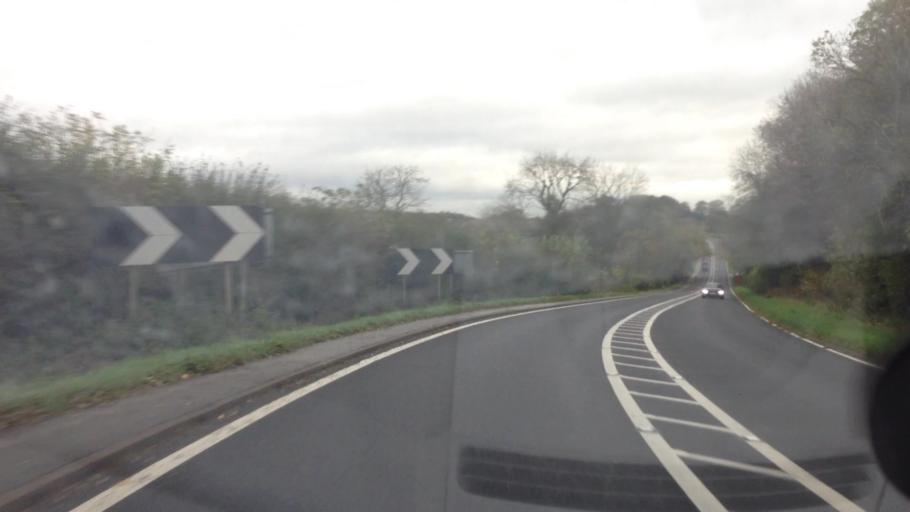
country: GB
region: England
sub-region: City and Borough of Leeds
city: Shadwell
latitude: 53.8558
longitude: -1.4615
